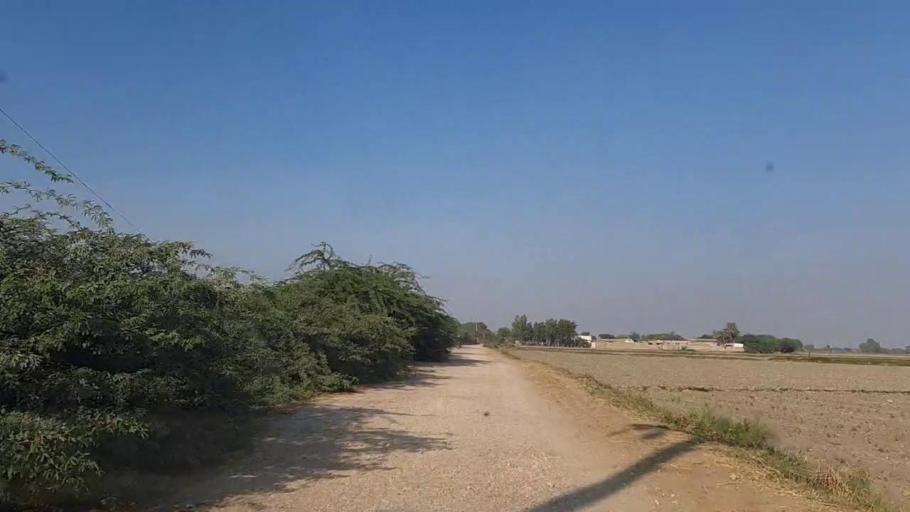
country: PK
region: Sindh
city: Thatta
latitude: 24.7565
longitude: 67.9617
